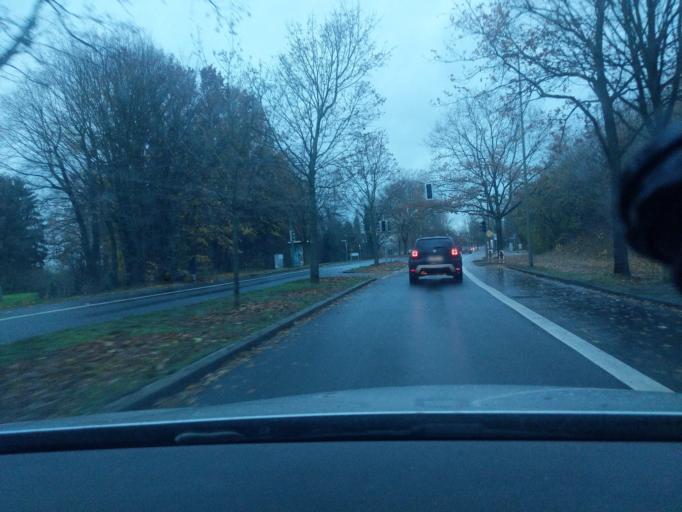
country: DE
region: North Rhine-Westphalia
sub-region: Regierungsbezirk Arnsberg
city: Hamm
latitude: 51.6672
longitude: 7.8519
